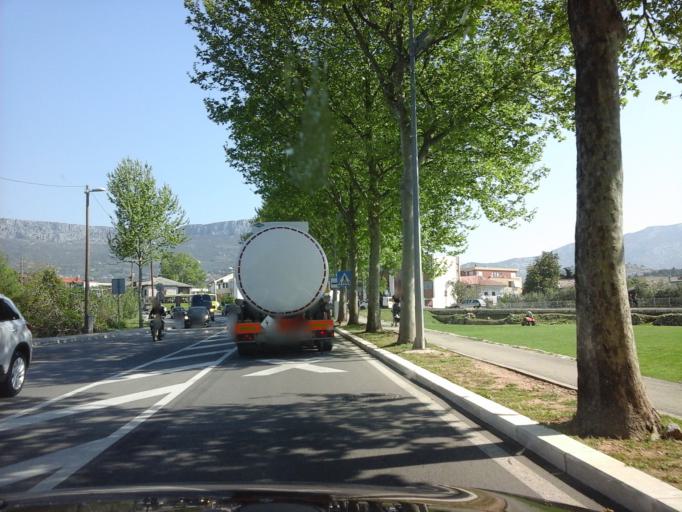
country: HR
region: Splitsko-Dalmatinska
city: Solin
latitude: 43.5402
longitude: 16.4909
